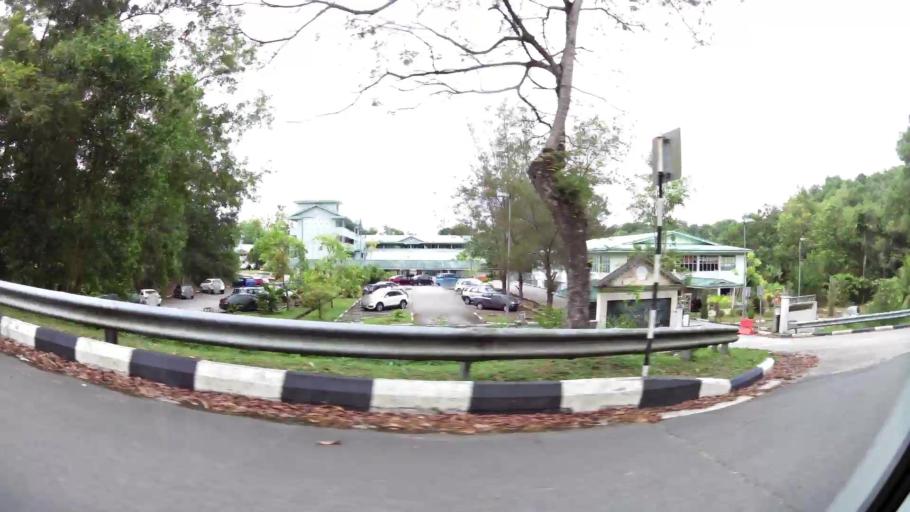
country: BN
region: Brunei and Muara
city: Bandar Seri Begawan
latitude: 4.8775
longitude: 114.8969
